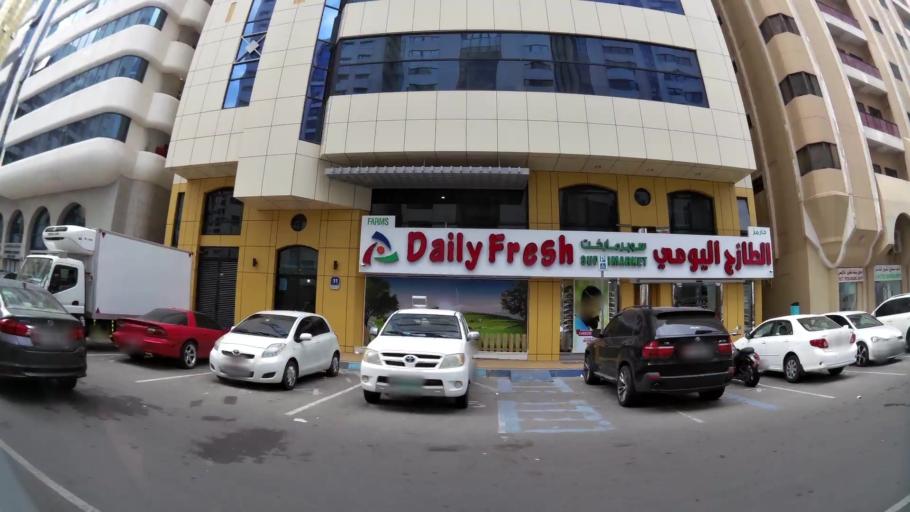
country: AE
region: Abu Dhabi
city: Abu Dhabi
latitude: 24.4923
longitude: 54.3600
